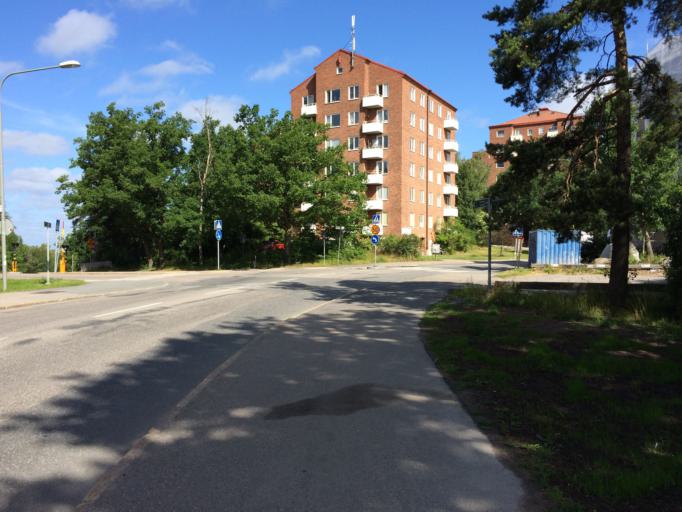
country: SE
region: Stockholm
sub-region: Huddinge Kommun
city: Segeltorp
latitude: 59.2994
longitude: 17.9819
